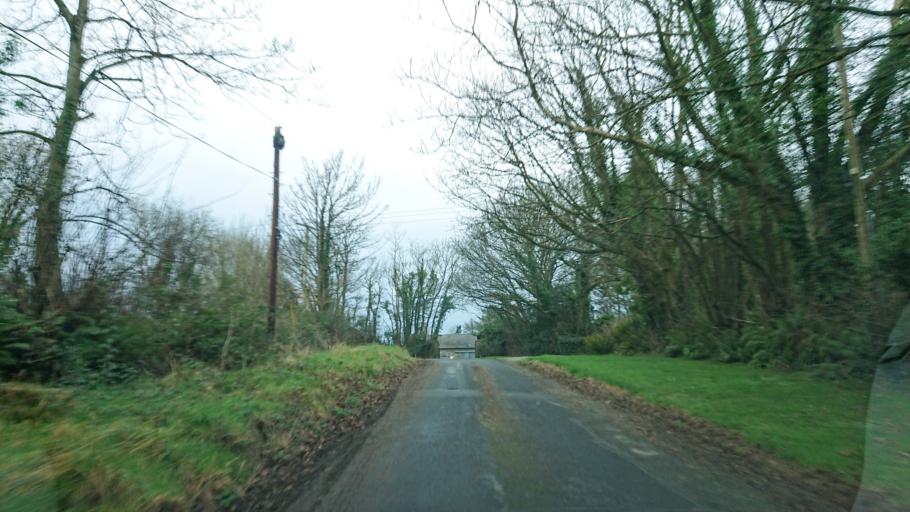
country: IE
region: Leinster
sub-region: Kilkenny
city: Mooncoin
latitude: 52.2301
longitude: -7.2517
